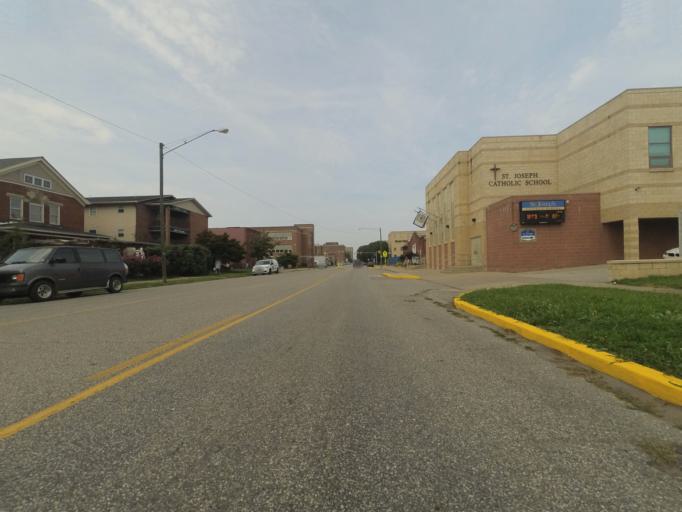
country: US
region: West Virginia
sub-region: Cabell County
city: Huntington
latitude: 38.4195
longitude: -82.4348
